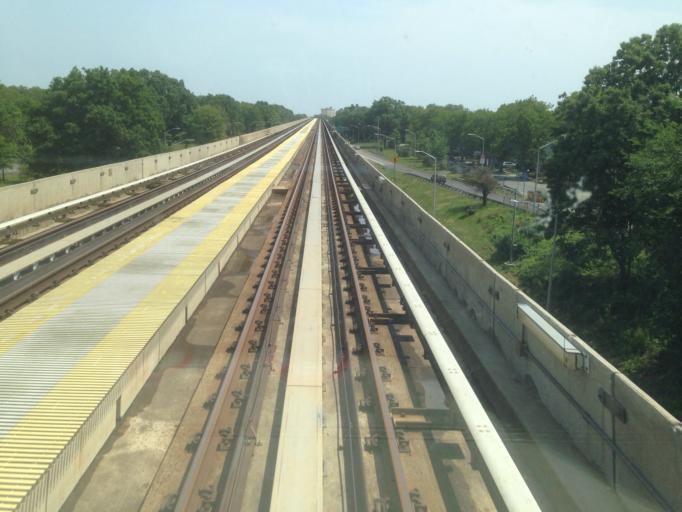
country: US
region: New York
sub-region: Queens County
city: Jamaica
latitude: 40.6825
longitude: -73.8058
